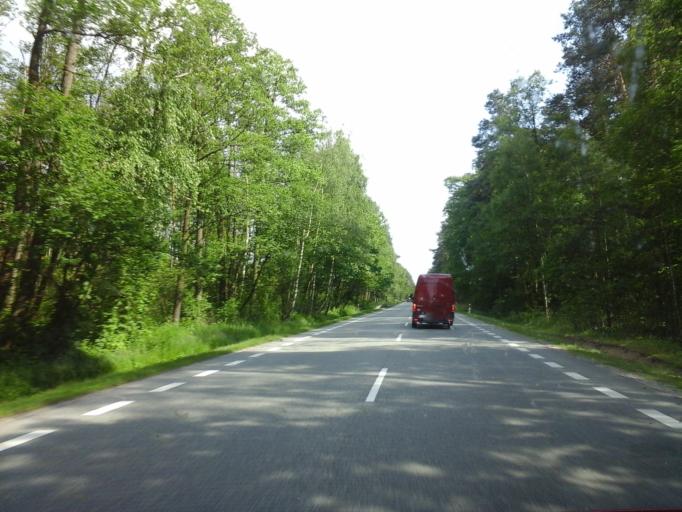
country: PL
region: Swietokrzyskie
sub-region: Powiat konecki
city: Ruda Maleniecka
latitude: 51.1626
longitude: 20.2270
